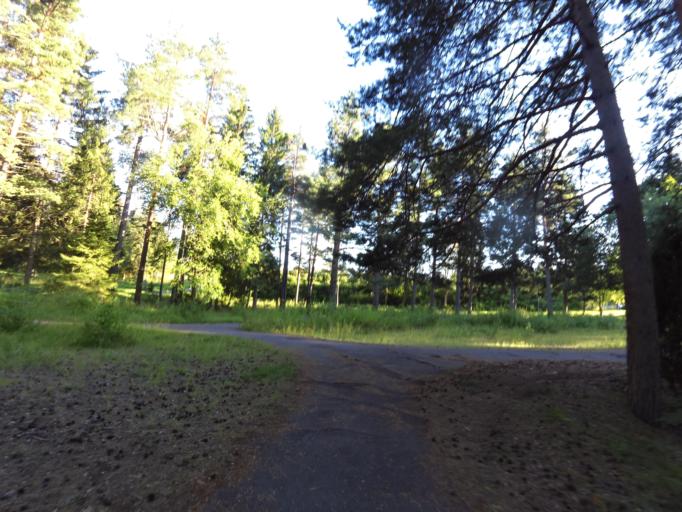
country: SE
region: Gaevleborg
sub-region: Gavle Kommun
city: Gavle
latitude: 60.6517
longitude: 17.1420
